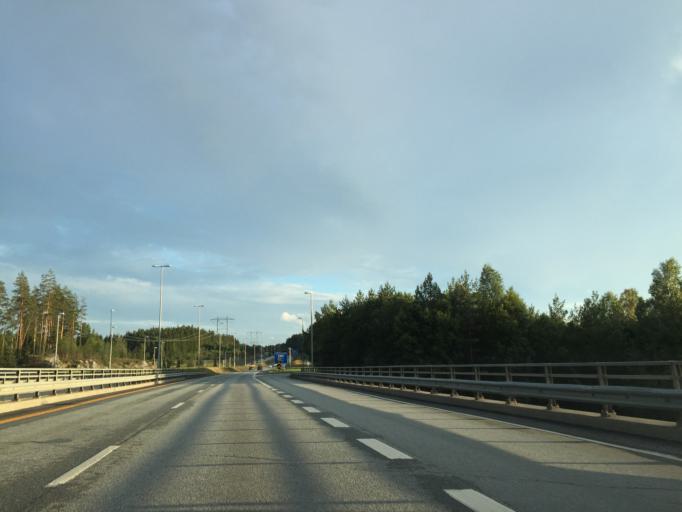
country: NO
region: Akershus
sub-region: Oppegard
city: Kolbotn
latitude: 59.7973
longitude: 10.8428
